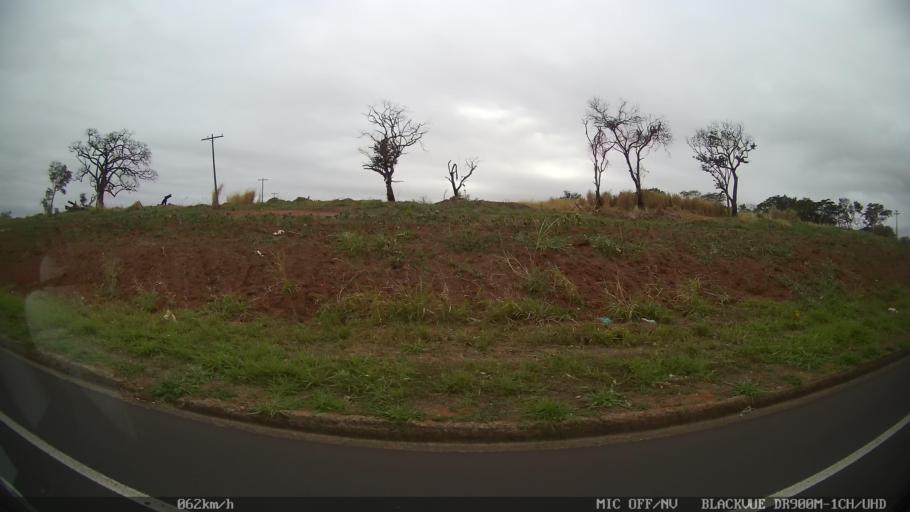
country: BR
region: Sao Paulo
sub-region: Sao Jose Do Rio Preto
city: Sao Jose do Rio Preto
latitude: -20.8299
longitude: -49.4280
